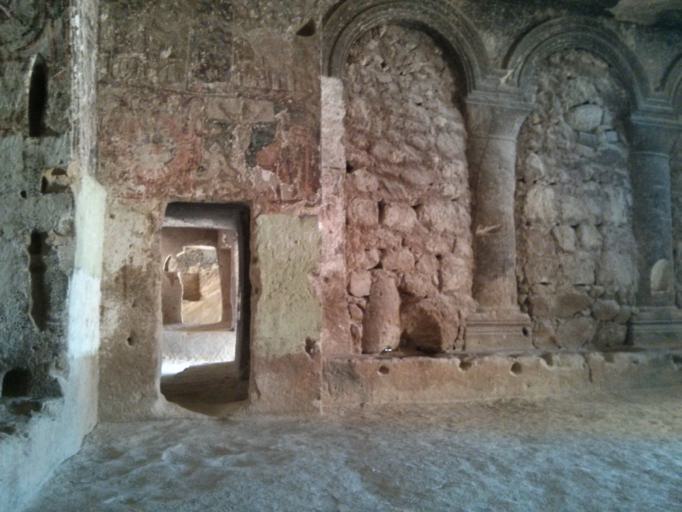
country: TR
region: Nevsehir
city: Goereme
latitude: 38.6676
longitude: 34.8431
